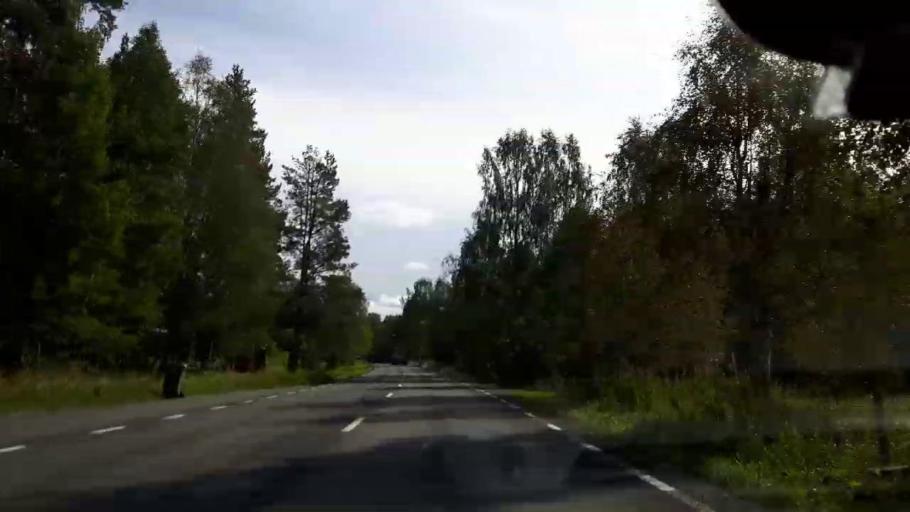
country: SE
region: Jaemtland
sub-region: Braecke Kommun
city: Braecke
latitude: 63.1653
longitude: 15.5600
